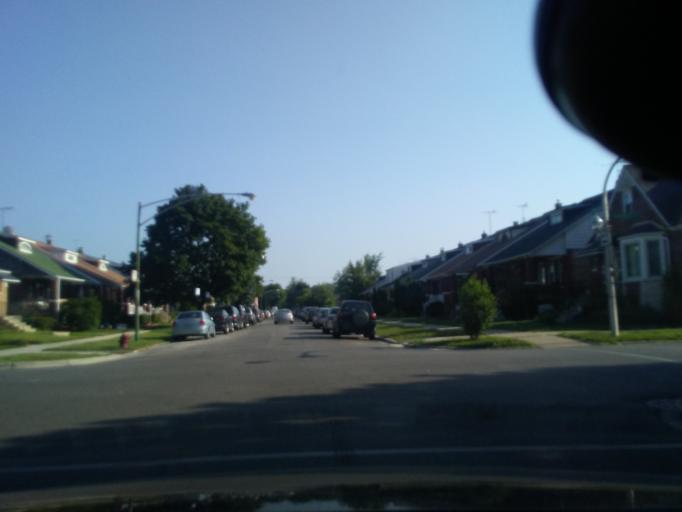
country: US
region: Illinois
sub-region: Cook County
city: Elmwood Park
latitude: 41.9292
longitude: -87.7687
